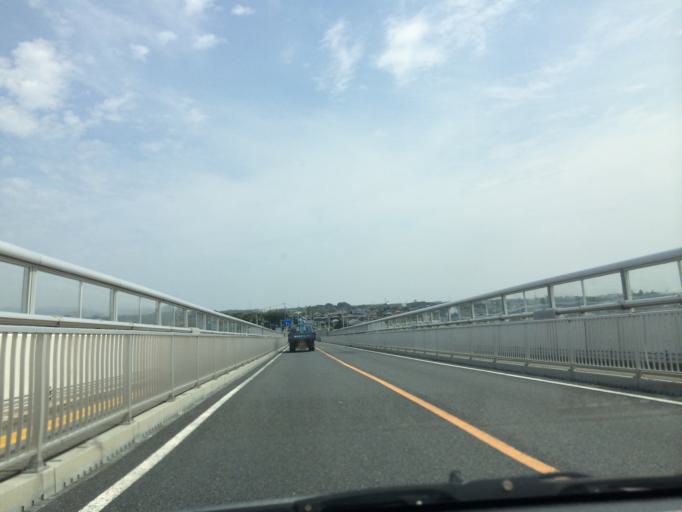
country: JP
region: Shimane
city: Sakaiminato
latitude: 35.5209
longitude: 133.2062
